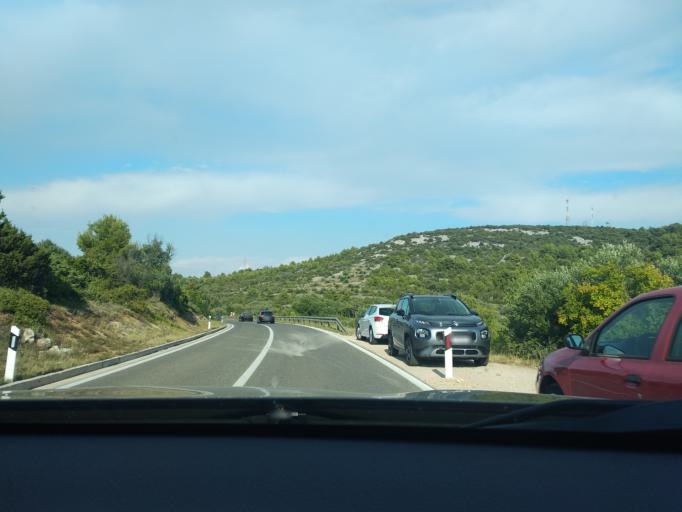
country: HR
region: Sibensko-Kniniska
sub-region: Grad Sibenik
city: Tisno
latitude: 43.8014
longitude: 15.6597
